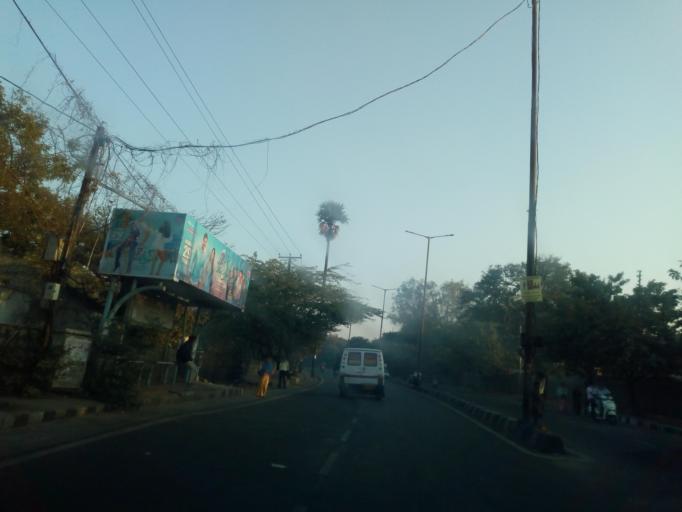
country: IN
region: Telangana
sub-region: Hyderabad
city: Malkajgiri
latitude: 17.4139
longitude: 78.5216
